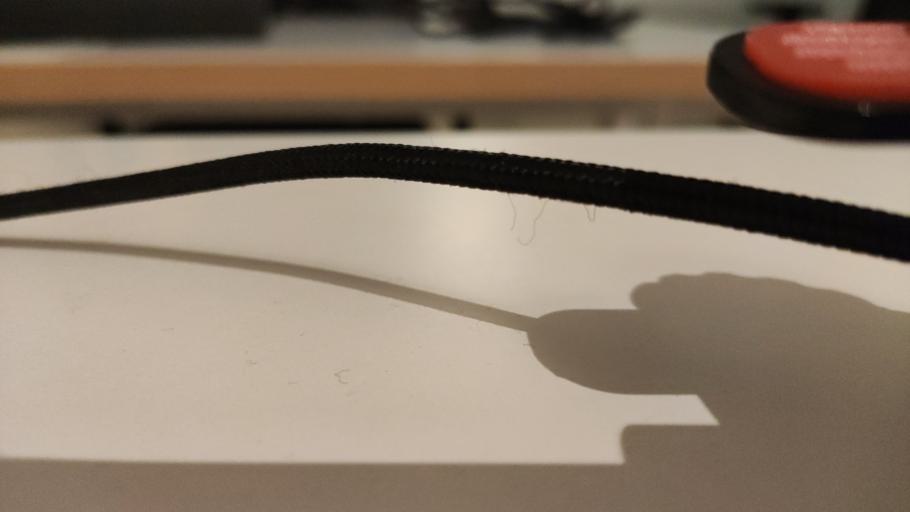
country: RU
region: Moskovskaya
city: Kurovskoye
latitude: 55.5989
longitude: 38.9251
